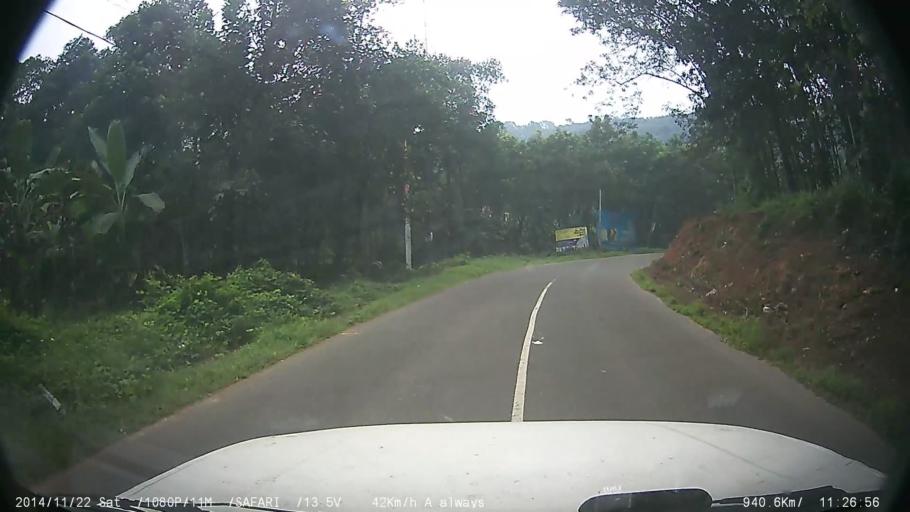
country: IN
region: Kerala
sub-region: Ernakulam
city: Muvattupuzha
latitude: 9.9343
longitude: 76.5743
